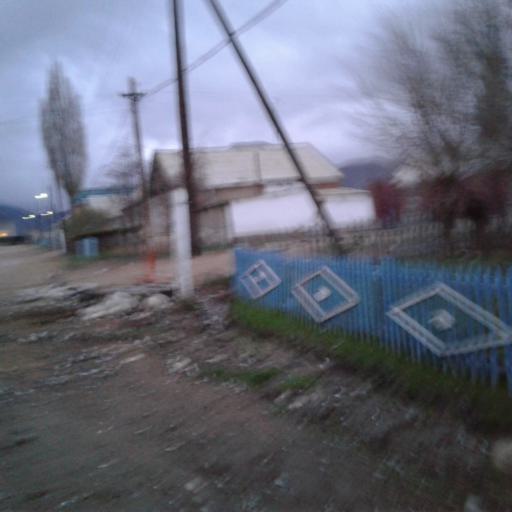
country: KG
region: Ysyk-Koel
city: Bokombayevskoye
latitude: 42.1093
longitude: 76.9860
